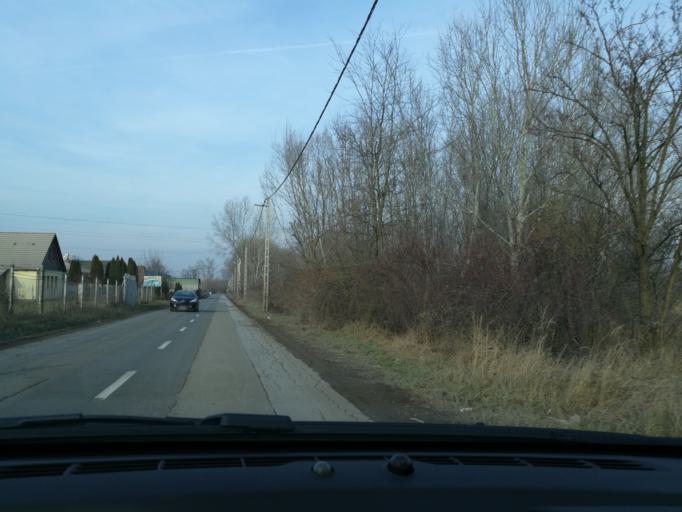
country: HU
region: Szabolcs-Szatmar-Bereg
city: Nyiregyhaza
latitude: 47.9355
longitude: 21.7082
